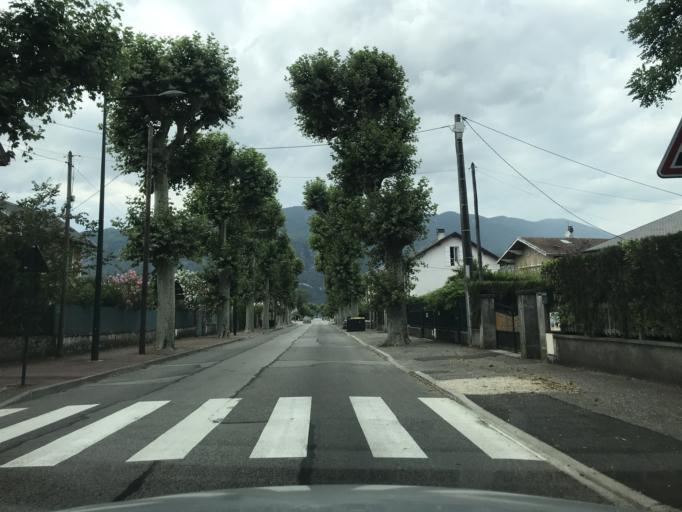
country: FR
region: Rhone-Alpes
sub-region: Departement de la Savoie
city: Brison-Saint-Innocent
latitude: 45.7045
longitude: 5.8931
